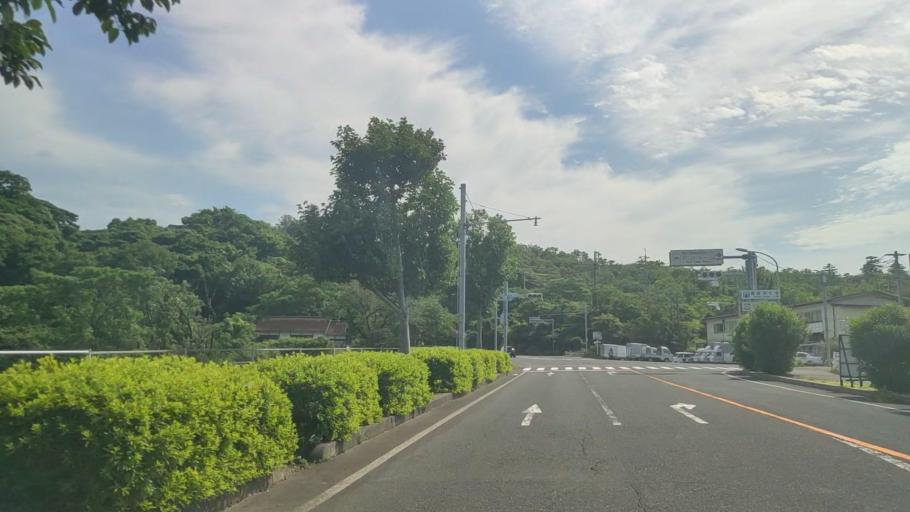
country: JP
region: Tottori
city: Tottori
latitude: 35.5340
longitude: 134.2311
